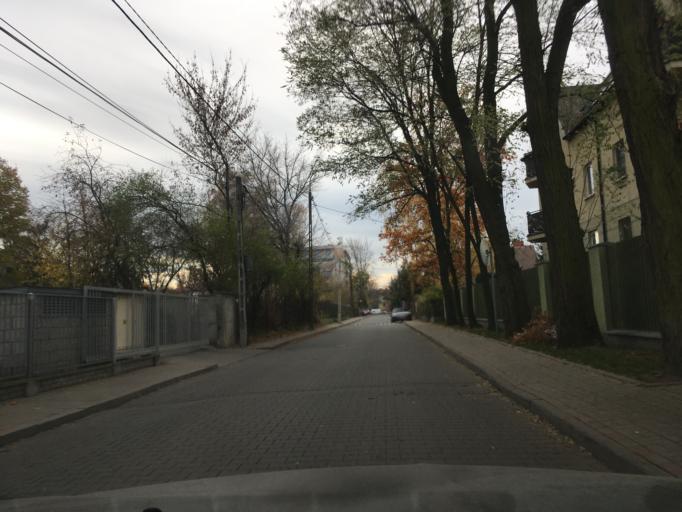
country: PL
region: Masovian Voivodeship
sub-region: Powiat piaseczynski
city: Piaseczno
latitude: 52.0703
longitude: 21.0227
